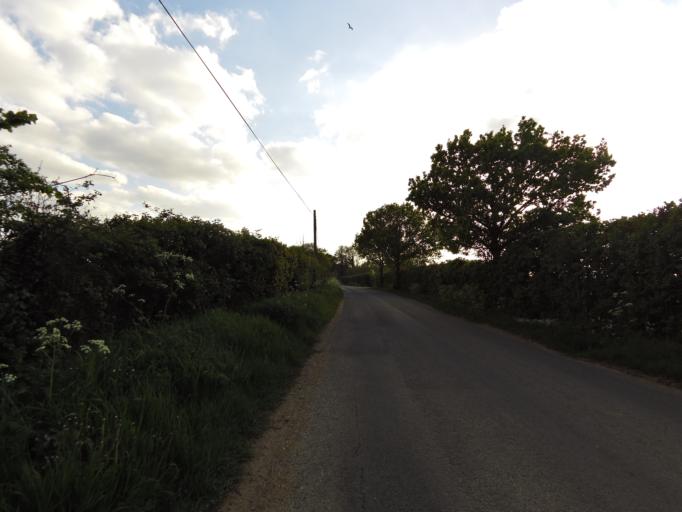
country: GB
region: England
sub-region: Suffolk
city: Beccles
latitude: 52.4227
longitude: 1.5151
